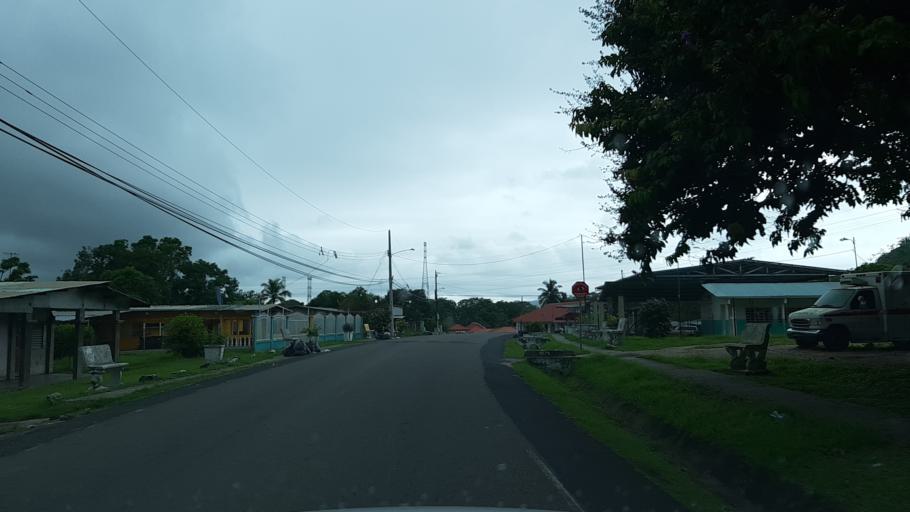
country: PA
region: Colon
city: Nuevo San Juan
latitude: 9.2406
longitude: -79.6585
